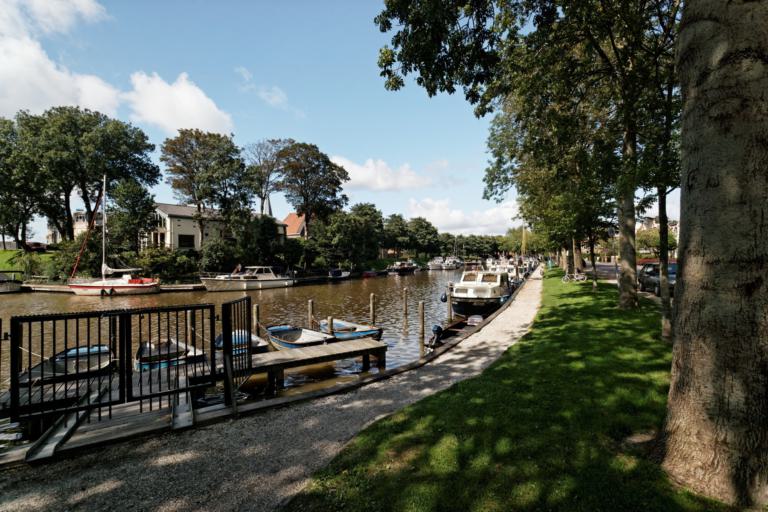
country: NL
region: Friesland
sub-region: Gemeente Harlingen
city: Harlingen
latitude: 53.1714
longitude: 5.4250
